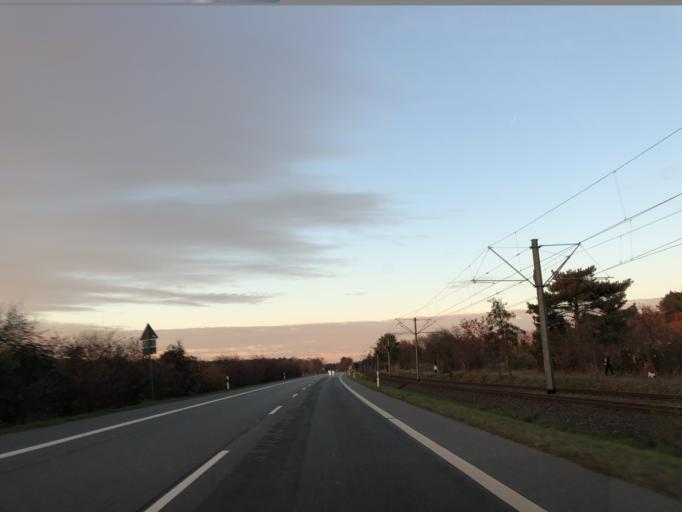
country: DE
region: Hesse
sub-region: Regierungsbezirk Darmstadt
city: Seeheim-Jugenheim
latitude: 49.7844
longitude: 8.6485
